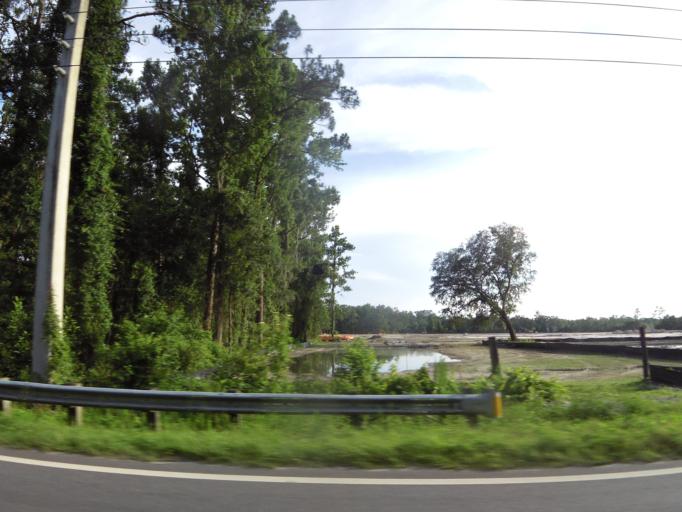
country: US
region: Florida
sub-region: Clay County
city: Green Cove Springs
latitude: 29.9794
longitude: -81.5179
